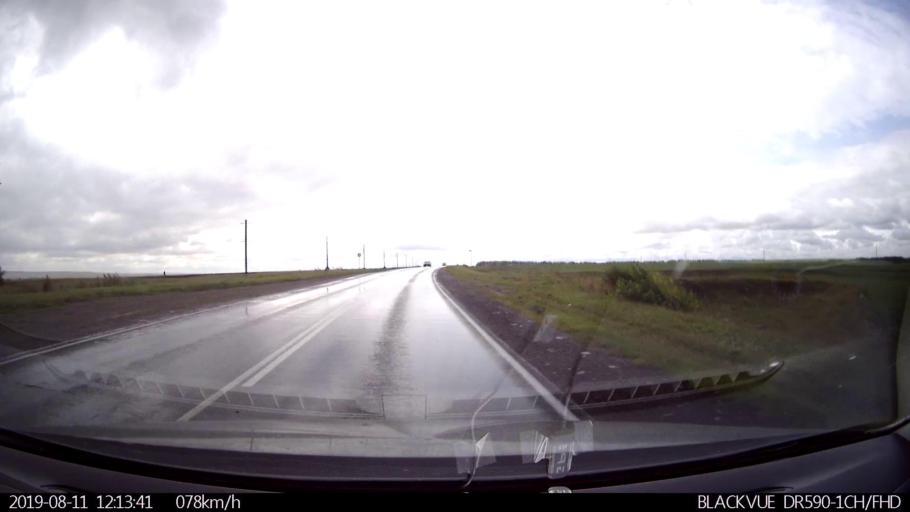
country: RU
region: Ulyanovsk
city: Ignatovka
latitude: 53.9595
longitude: 47.9898
